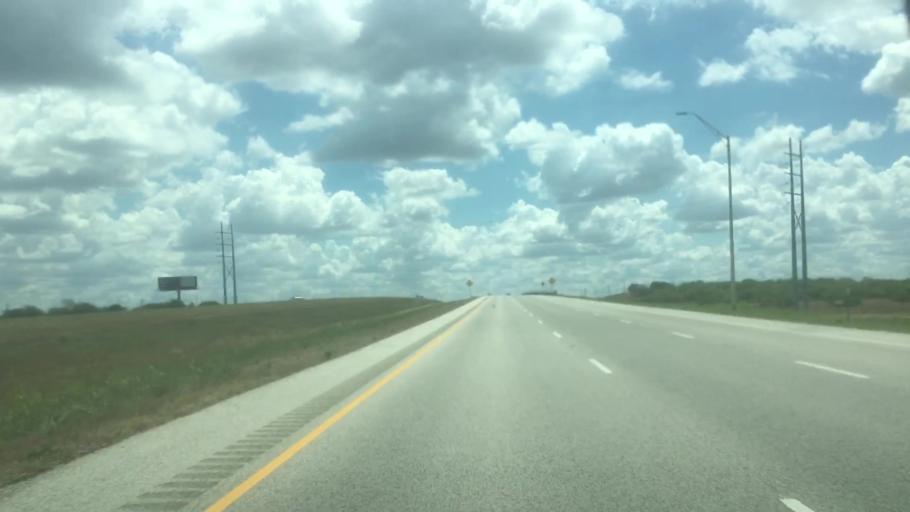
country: US
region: Texas
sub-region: Caldwell County
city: Uhland
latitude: 30.0096
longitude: -97.6879
